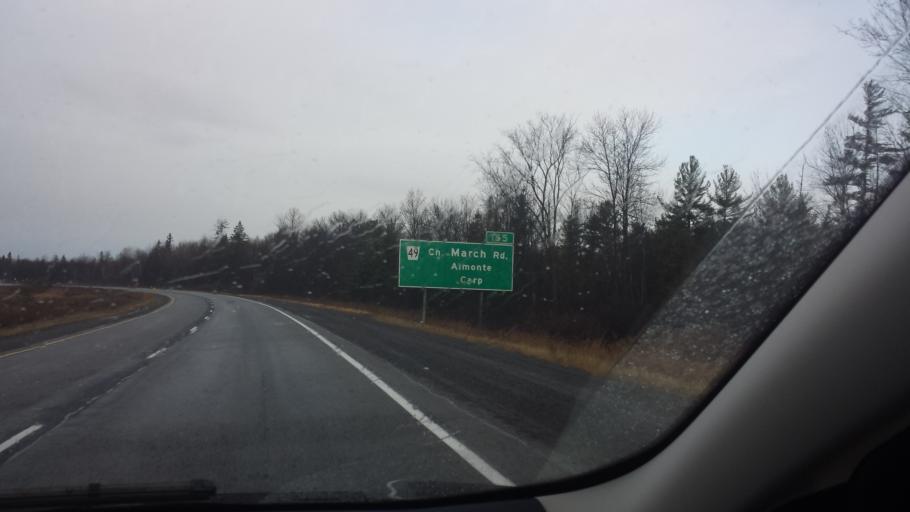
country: CA
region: Ontario
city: Carleton Place
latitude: 45.3080
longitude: -76.0378
